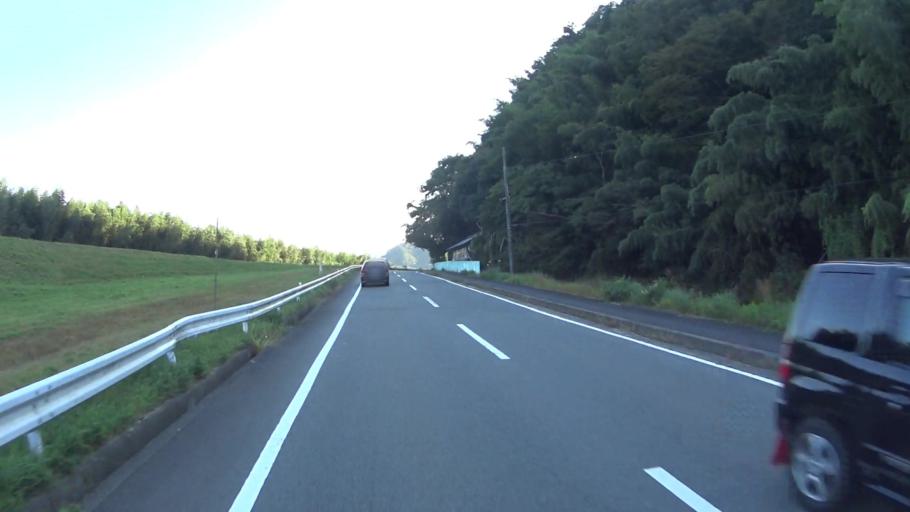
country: JP
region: Kyoto
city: Fukuchiyama
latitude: 35.3270
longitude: 135.1108
